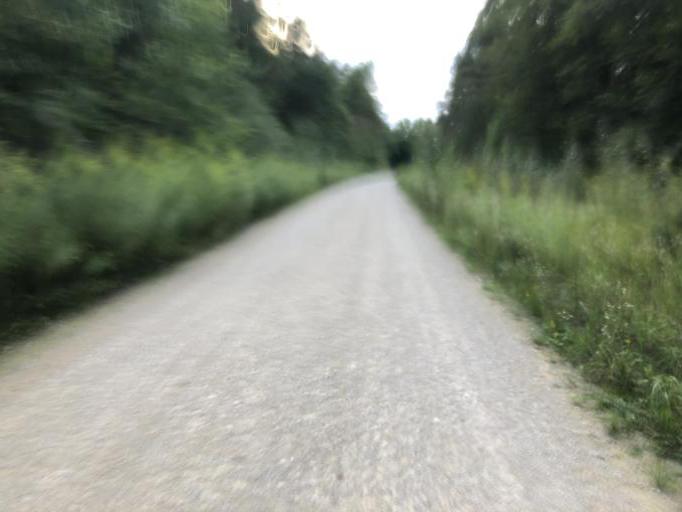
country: DE
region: Bavaria
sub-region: Regierungsbezirk Mittelfranken
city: Buckenhof
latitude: 49.5857
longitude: 11.0454
